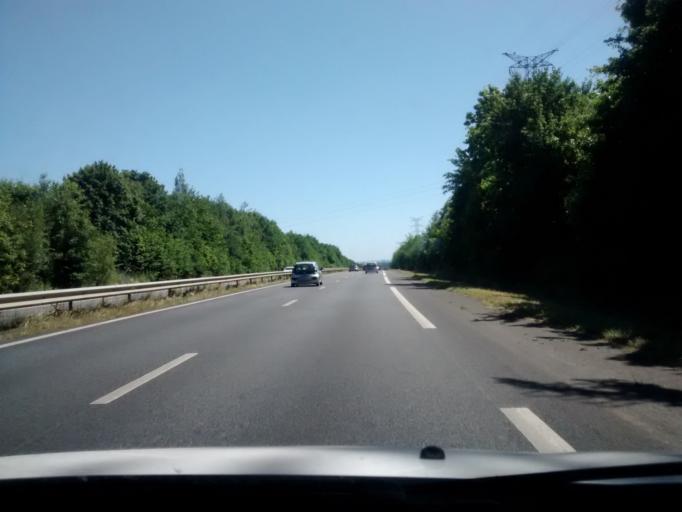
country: FR
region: Brittany
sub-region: Departement d'Ille-et-Vilaine
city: La Chapelle-des-Fougeretz
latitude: 48.1898
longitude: -1.7217
